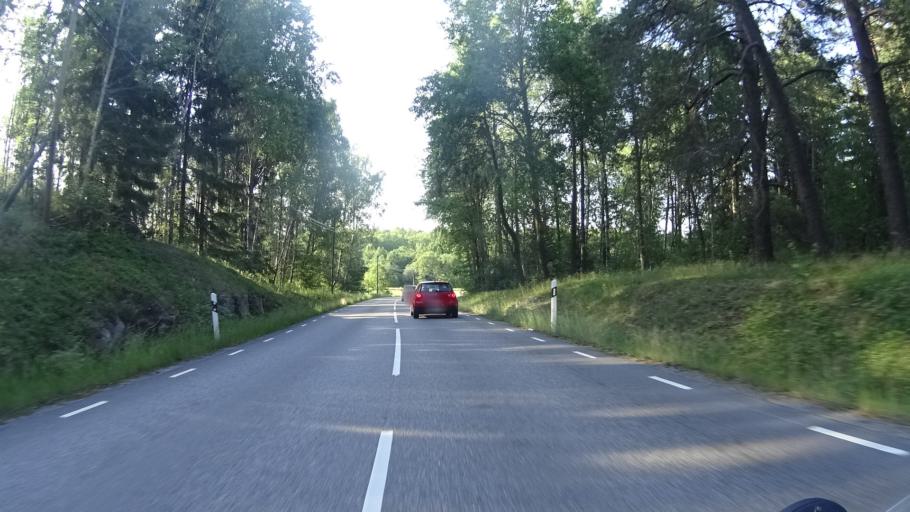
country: SE
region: Stockholm
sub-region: Sodertalje Kommun
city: Pershagen
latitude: 59.1054
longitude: 17.6354
